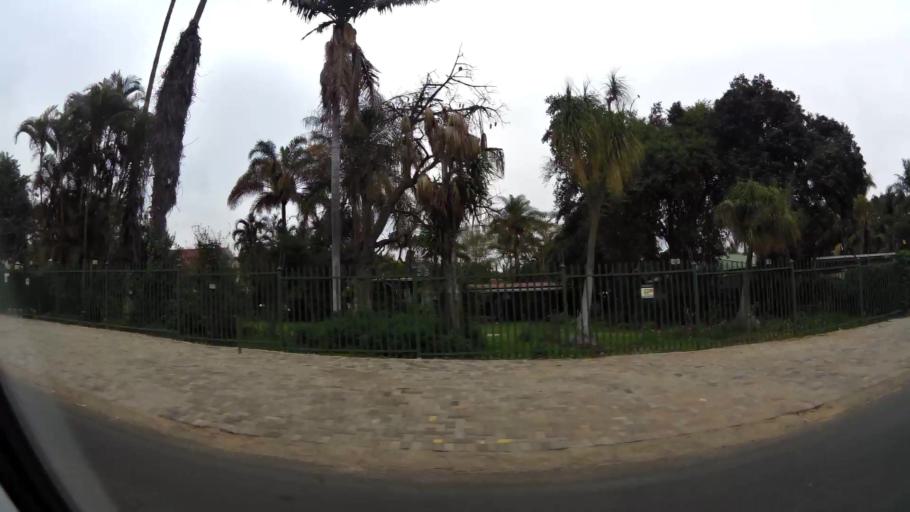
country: ZA
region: Limpopo
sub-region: Capricorn District Municipality
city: Polokwane
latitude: -23.8997
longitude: 29.4654
